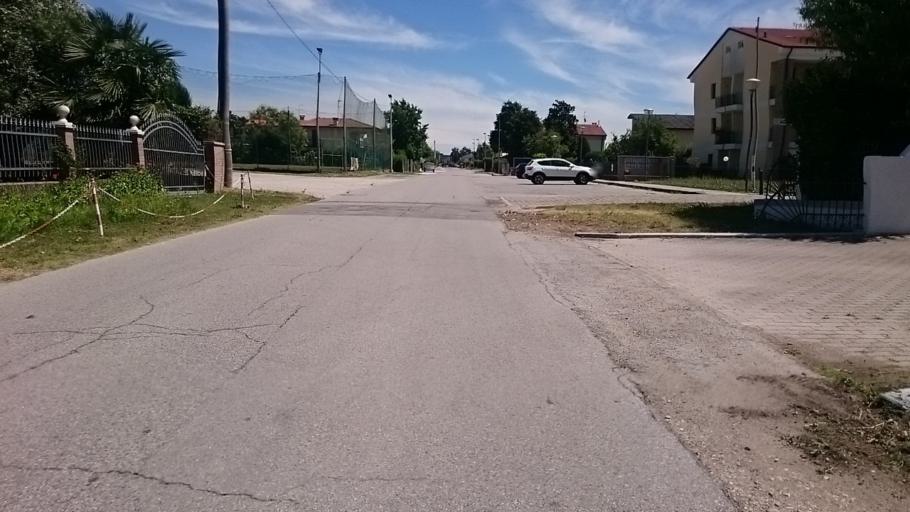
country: IT
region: Veneto
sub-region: Provincia di Padova
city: Borgoricco-San Michele delle Badesse-Sant'Eufemia
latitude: 45.5378
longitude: 11.9373
